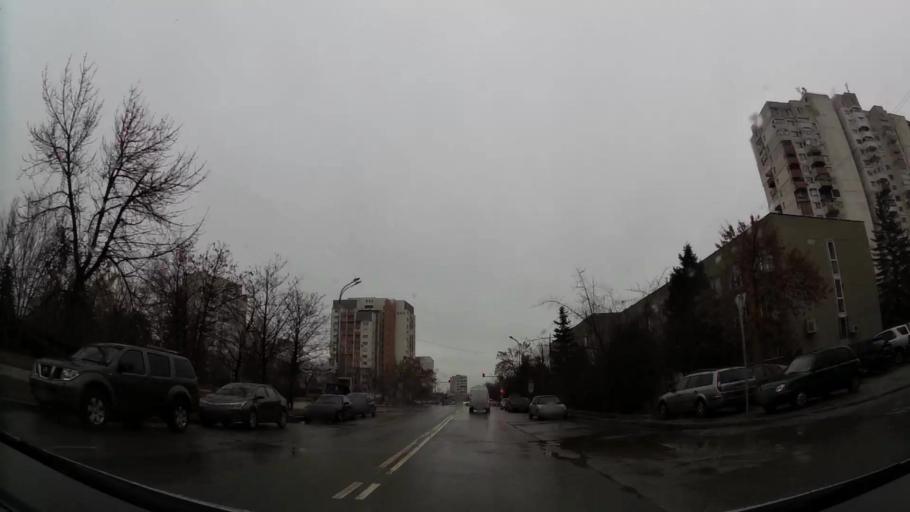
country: BG
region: Sofia-Capital
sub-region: Stolichna Obshtina
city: Sofia
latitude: 42.6407
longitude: 23.3802
